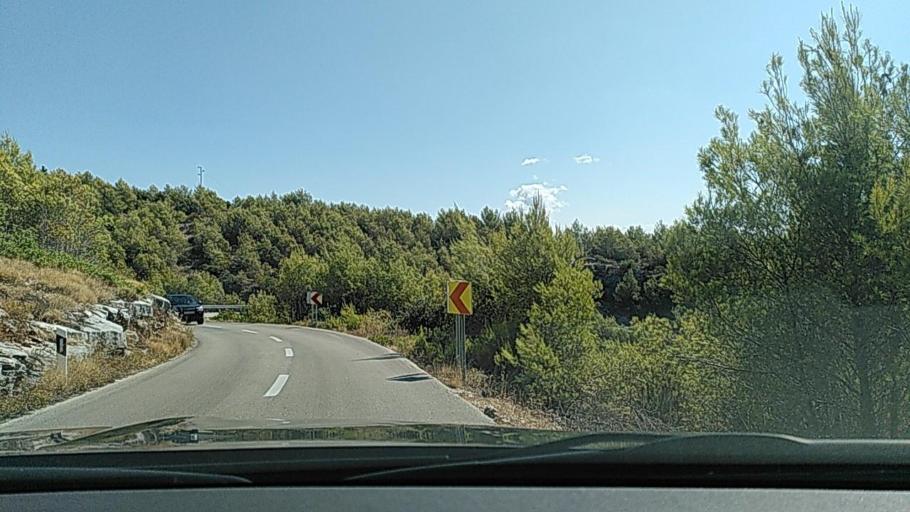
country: HR
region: Splitsko-Dalmatinska
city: Tucepi
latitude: 43.1325
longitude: 16.9792
